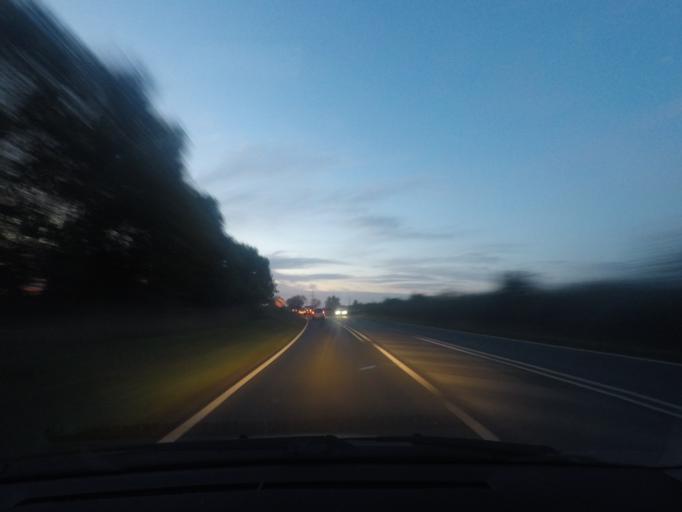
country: GB
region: England
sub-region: East Riding of Yorkshire
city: Wilberfoss
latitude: 53.9421
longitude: -0.8657
